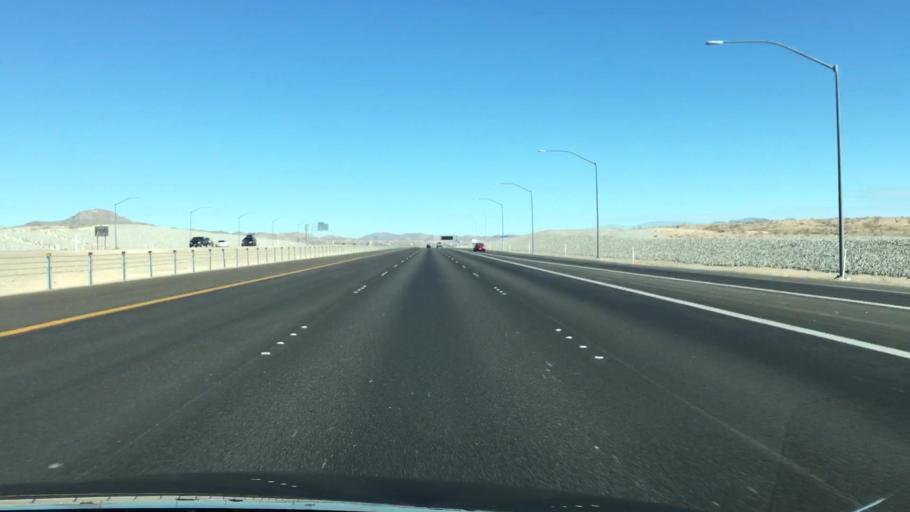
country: US
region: Nevada
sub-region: Clark County
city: Nellis Air Force Base
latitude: 36.2726
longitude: -115.0517
